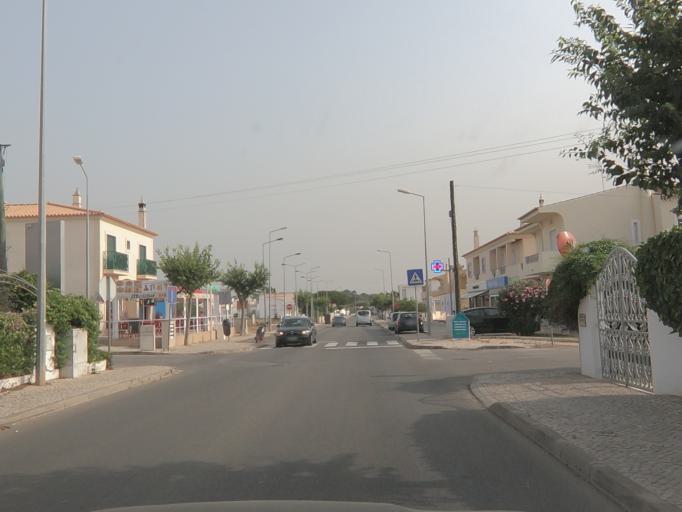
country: PT
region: Faro
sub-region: Albufeira
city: Guia
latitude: 37.0945
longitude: -8.3098
